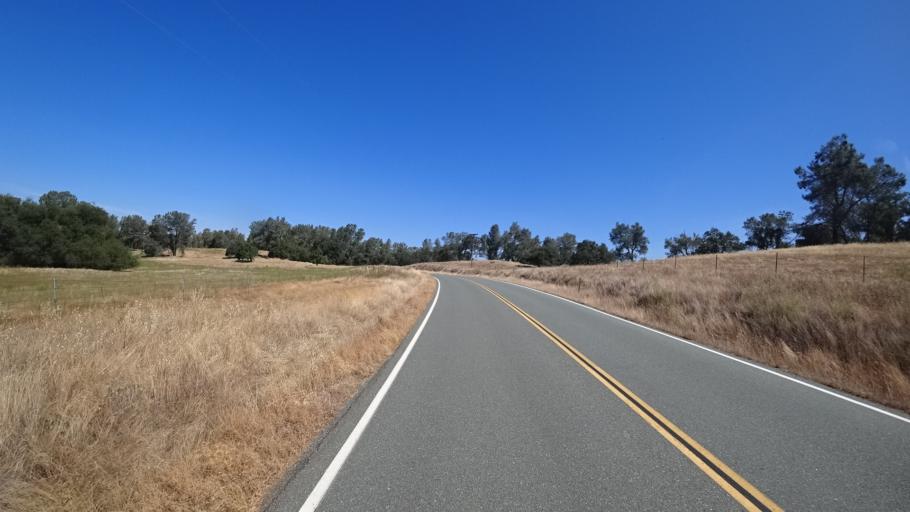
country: US
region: California
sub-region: Calaveras County
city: Valley Springs
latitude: 38.2229
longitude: -120.8845
